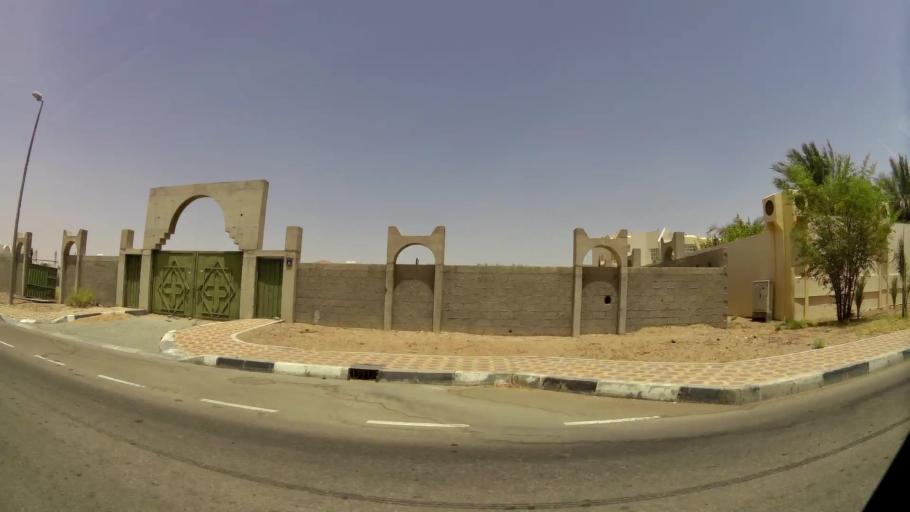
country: OM
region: Al Buraimi
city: Al Buraymi
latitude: 24.2644
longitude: 55.7063
